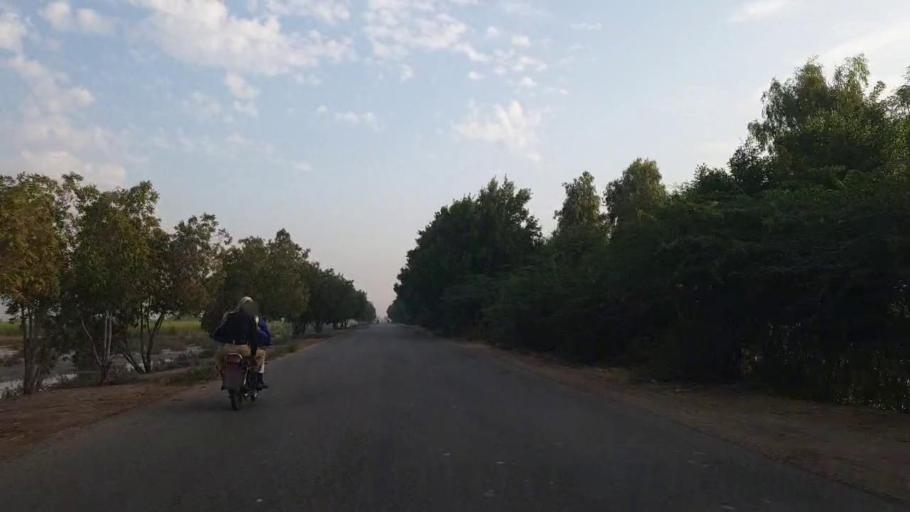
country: PK
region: Sindh
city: Badin
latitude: 24.6826
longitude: 68.9111
